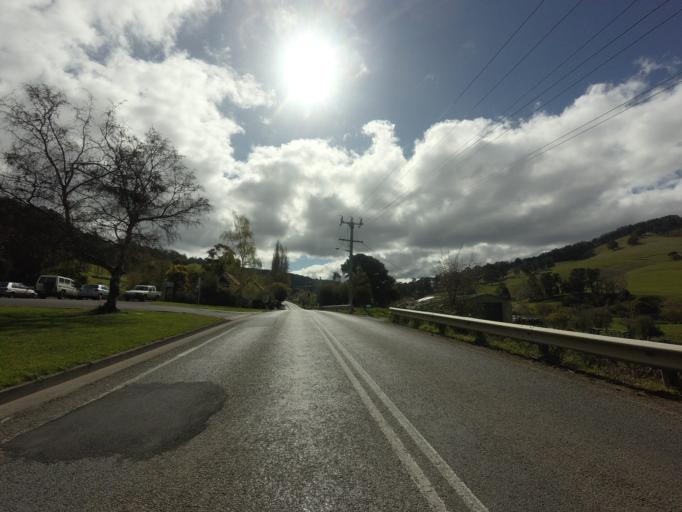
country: AU
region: Tasmania
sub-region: Huon Valley
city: Cygnet
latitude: -43.3102
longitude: 147.0135
